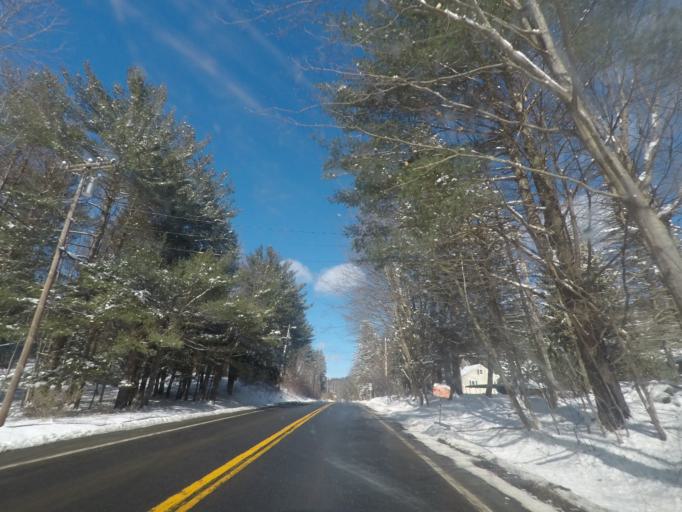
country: US
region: New York
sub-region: Rensselaer County
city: Averill Park
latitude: 42.5970
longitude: -73.5171
